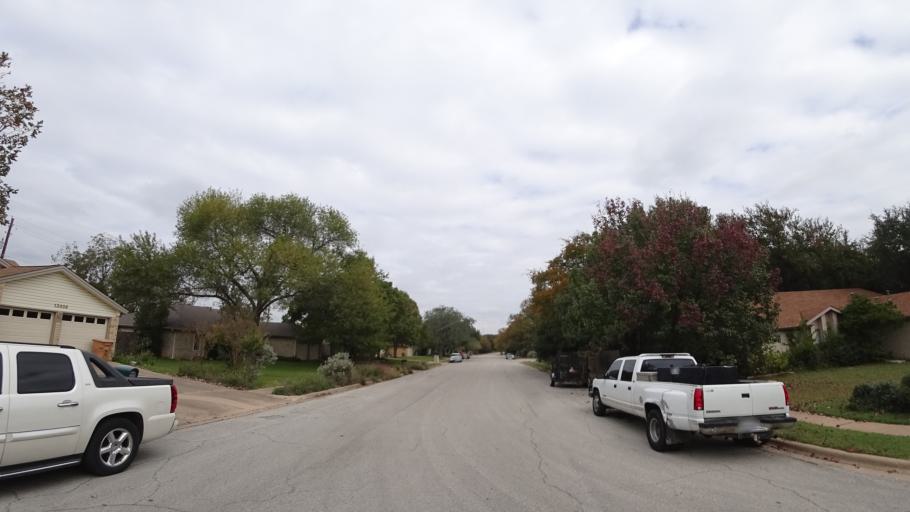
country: US
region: Texas
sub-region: Travis County
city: Wells Branch
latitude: 30.4324
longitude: -97.7183
